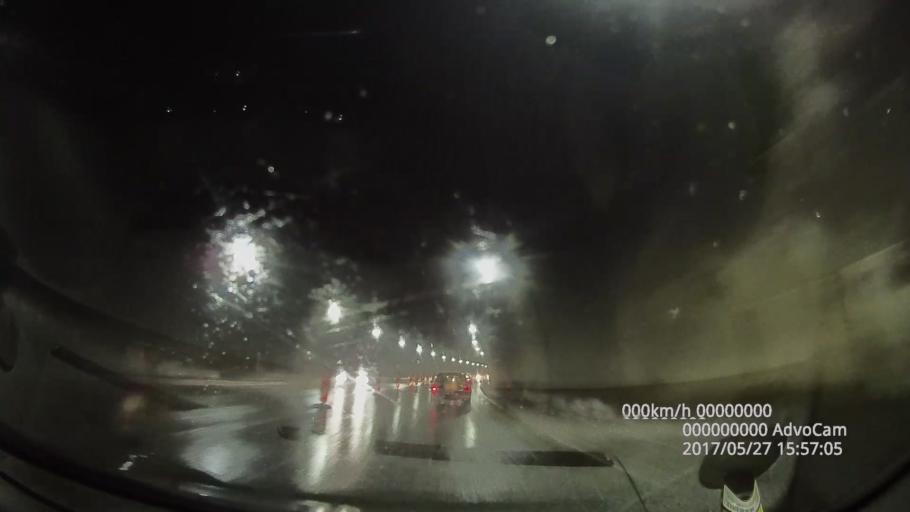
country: BG
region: Sofiya
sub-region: Obshtina Botevgrad
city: Botevgrad
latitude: 42.8566
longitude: 23.7908
